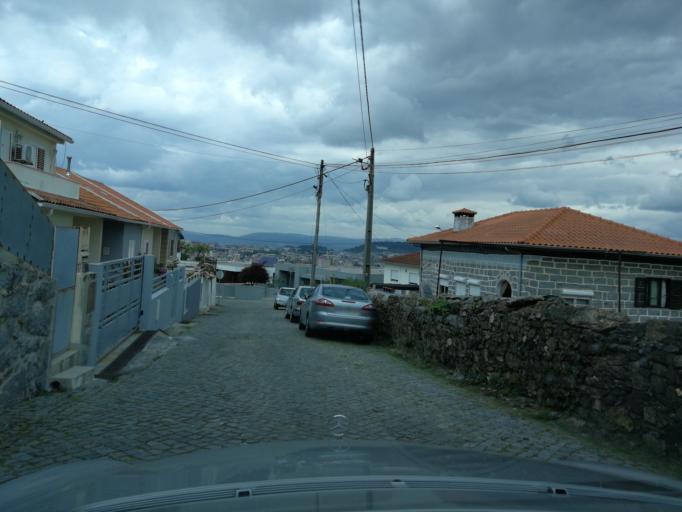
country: PT
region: Braga
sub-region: Braga
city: Braga
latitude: 41.5348
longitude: -8.3988
